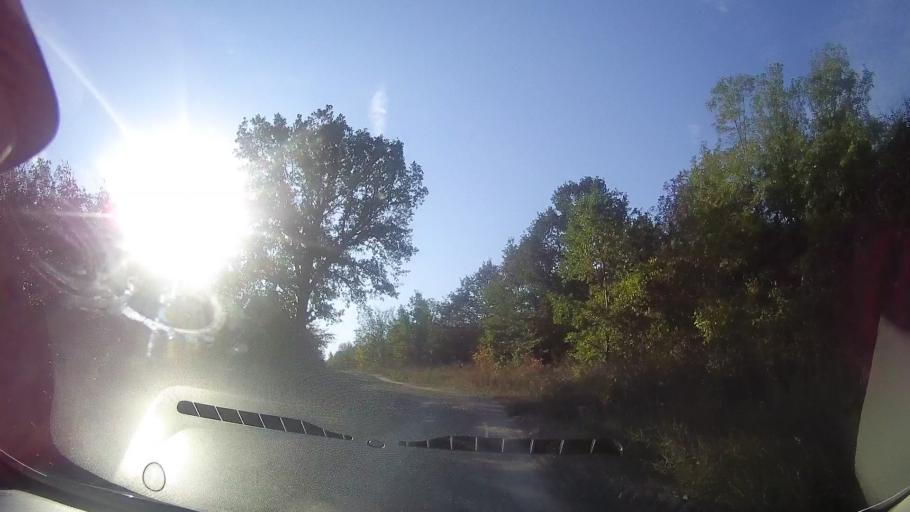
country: RO
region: Timis
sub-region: Comuna Bogda
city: Bogda
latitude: 45.9495
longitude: 21.6178
